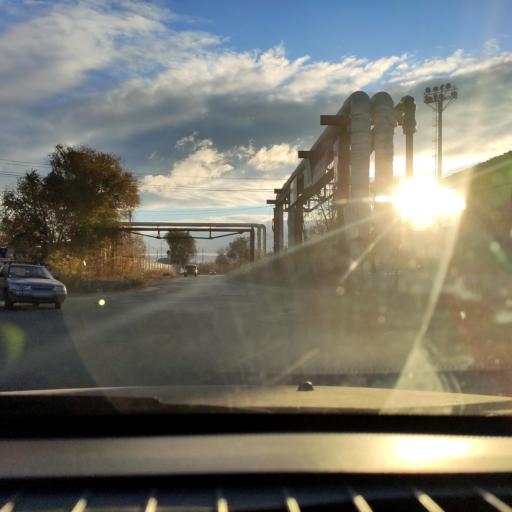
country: RU
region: Samara
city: Tol'yatti
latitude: 53.5754
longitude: 49.2833
